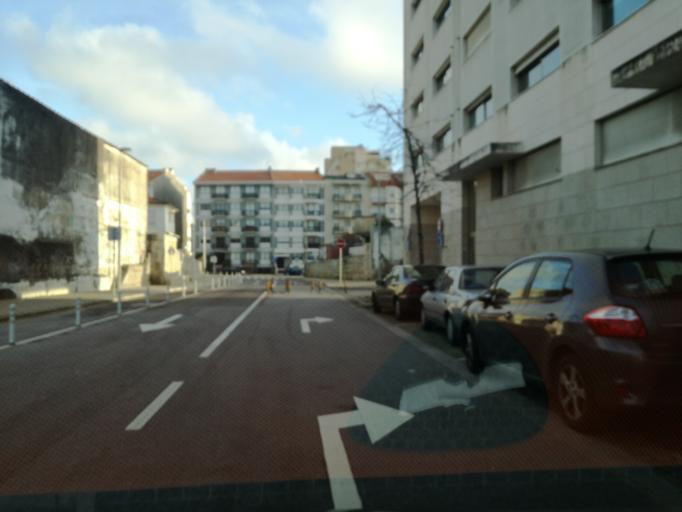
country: PT
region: Porto
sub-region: Porto
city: Porto
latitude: 41.1658
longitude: -8.6313
